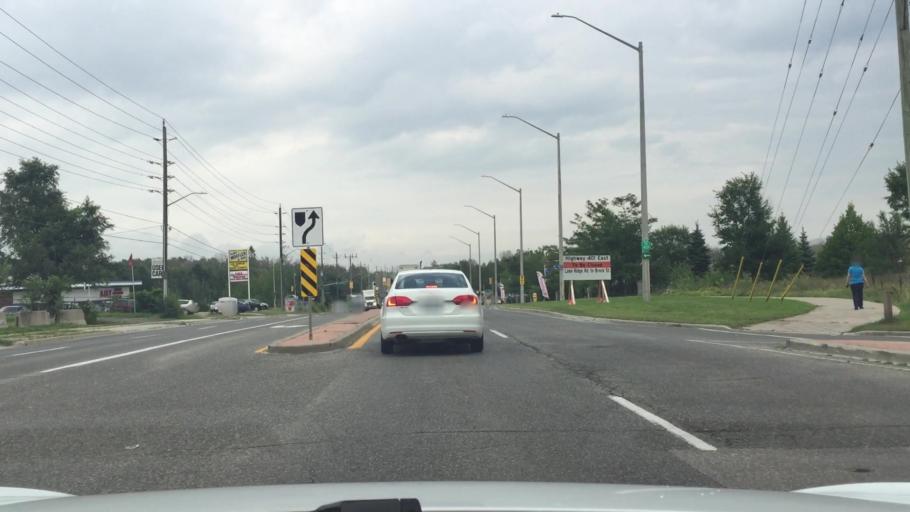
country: CA
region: Ontario
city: Ajax
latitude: 43.8462
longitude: -79.0085
